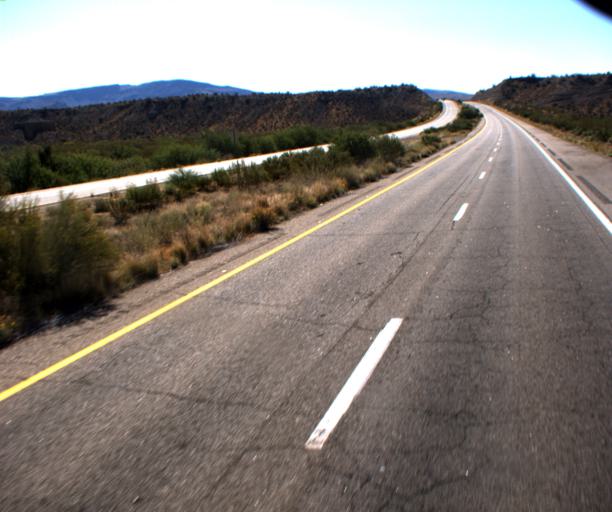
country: US
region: Arizona
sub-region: Yavapai County
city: Bagdad
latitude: 34.6396
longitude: -113.5616
